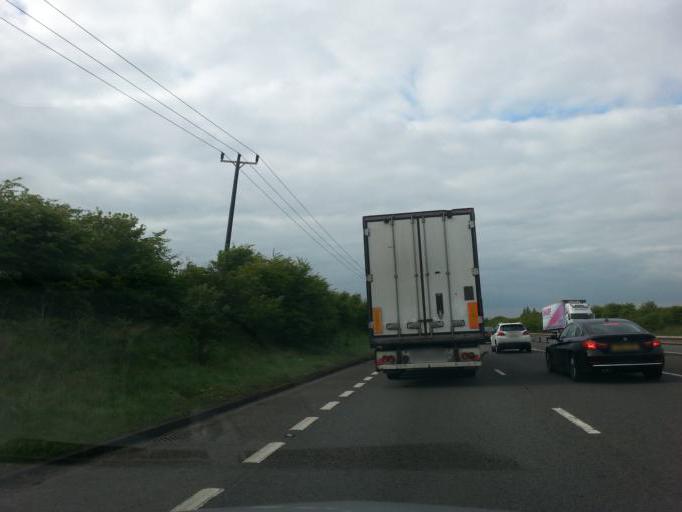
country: GB
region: England
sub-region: Lincolnshire
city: Long Bennington
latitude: 53.0375
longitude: -0.7756
